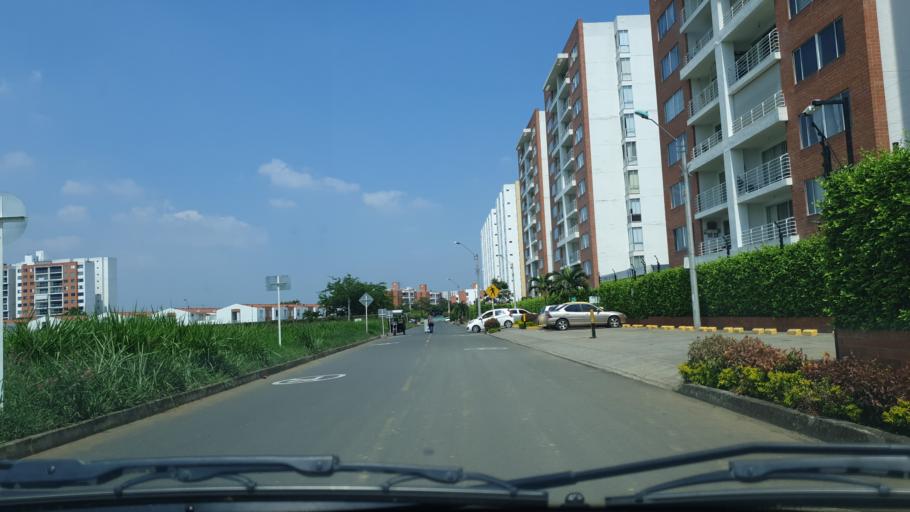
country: CO
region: Valle del Cauca
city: Cali
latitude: 3.3657
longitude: -76.5228
